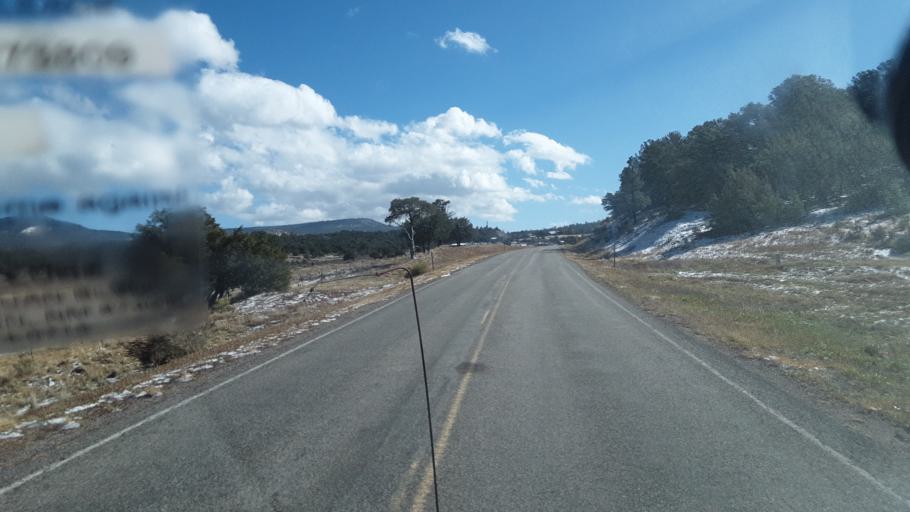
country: US
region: New Mexico
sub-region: Rio Arriba County
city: Santa Teresa
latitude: 36.2346
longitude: -106.8419
